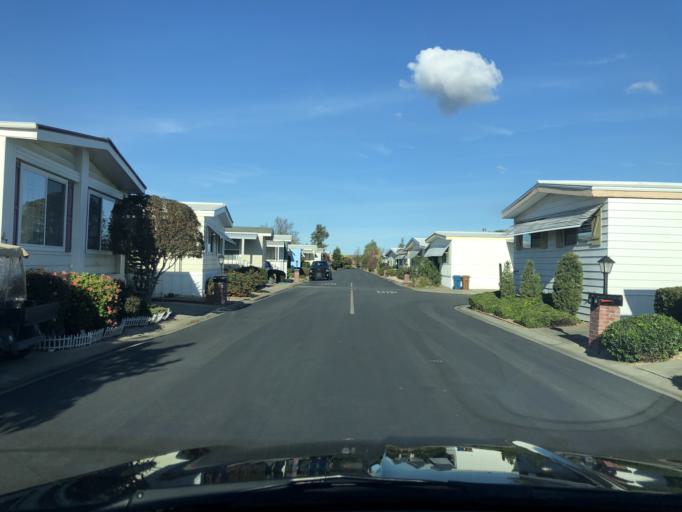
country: US
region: California
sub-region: Contra Costa County
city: Pacheco
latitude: 37.9932
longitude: -122.0660
